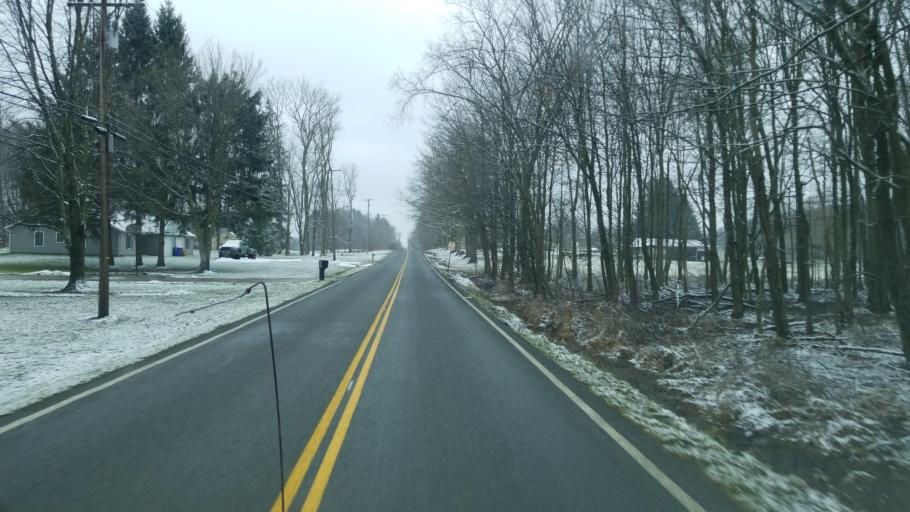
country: US
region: Ohio
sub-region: Portage County
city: Mantua
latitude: 41.3004
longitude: -81.2455
